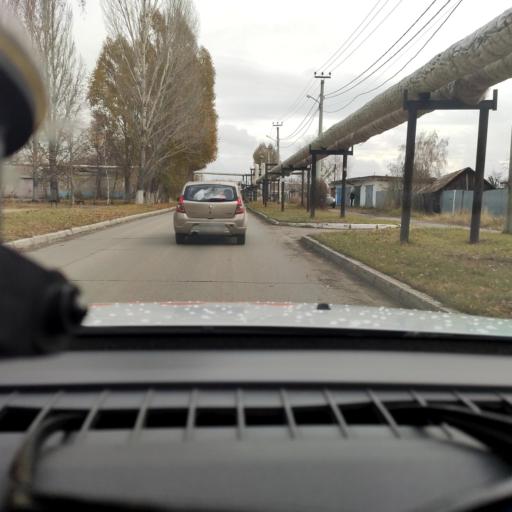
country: RU
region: Samara
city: Chapayevsk
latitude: 52.9834
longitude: 49.7205
